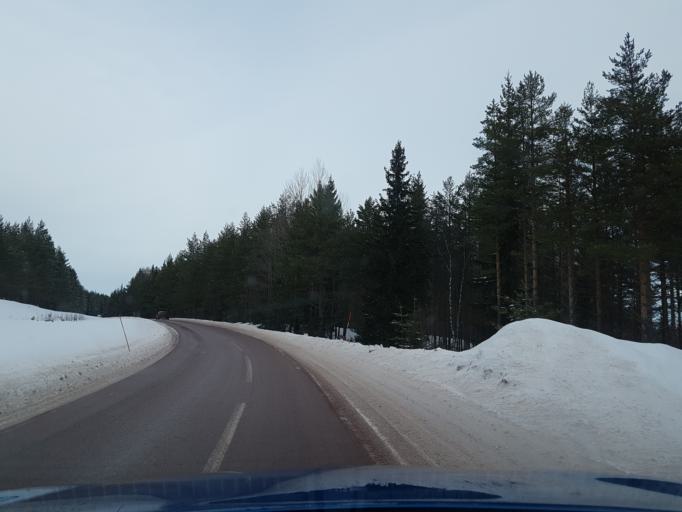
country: SE
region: Dalarna
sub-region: Orsa Kommun
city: Orsa
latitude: 61.1622
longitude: 14.6632
